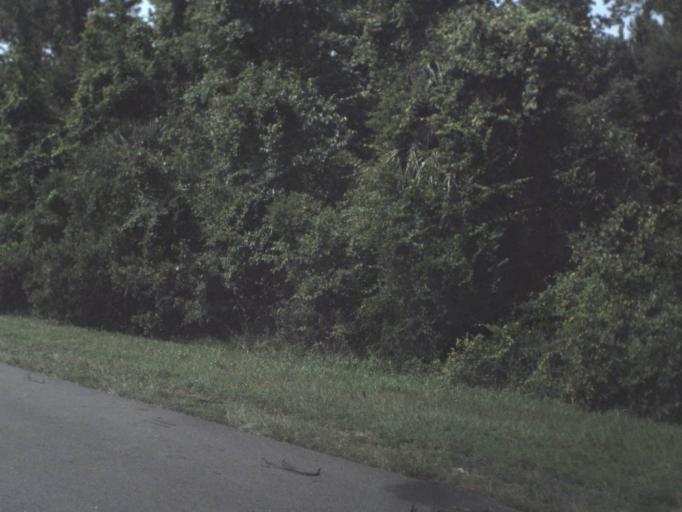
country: US
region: Florida
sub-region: Nassau County
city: Yulee
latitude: 30.5603
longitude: -81.6423
